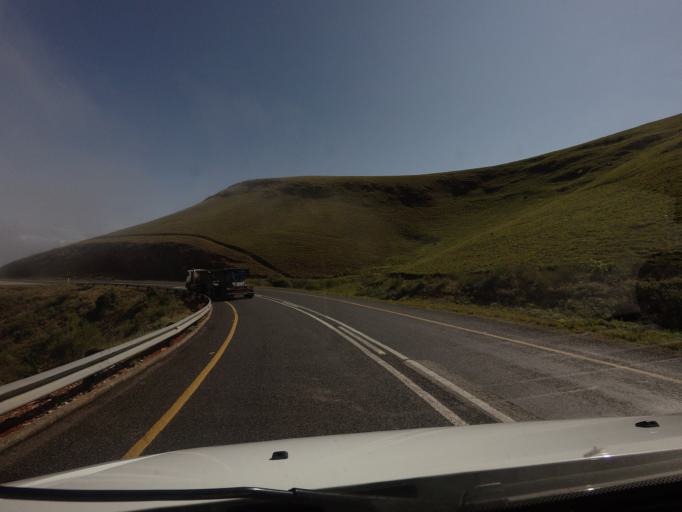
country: ZA
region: Mpumalanga
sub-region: Ehlanzeni District
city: Lydenburg
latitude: -25.1601
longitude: 30.6283
